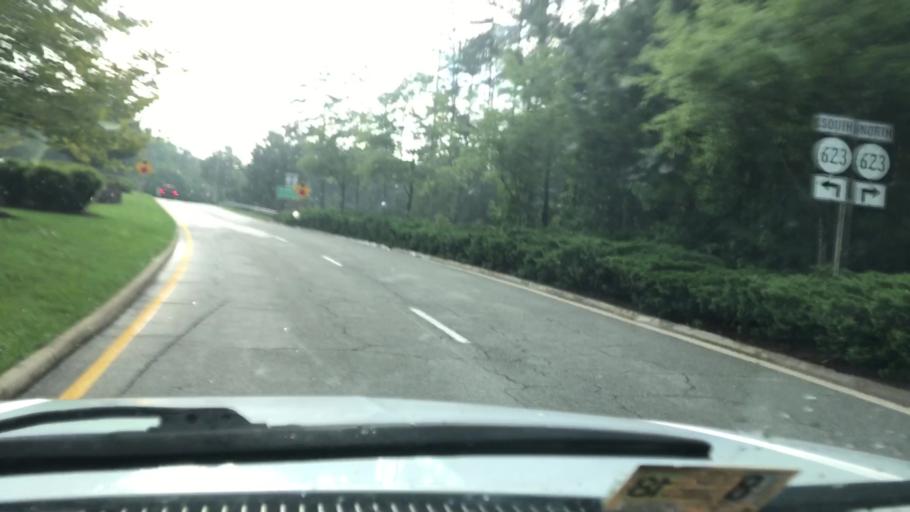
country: US
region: Virginia
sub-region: Henrico County
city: Short Pump
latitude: 37.6381
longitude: -77.6767
